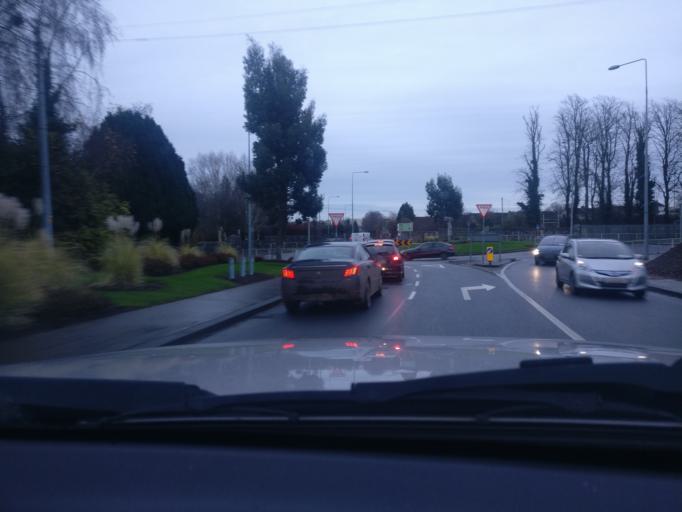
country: IE
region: Leinster
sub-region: An Mhi
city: Navan
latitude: 53.6546
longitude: -6.6993
